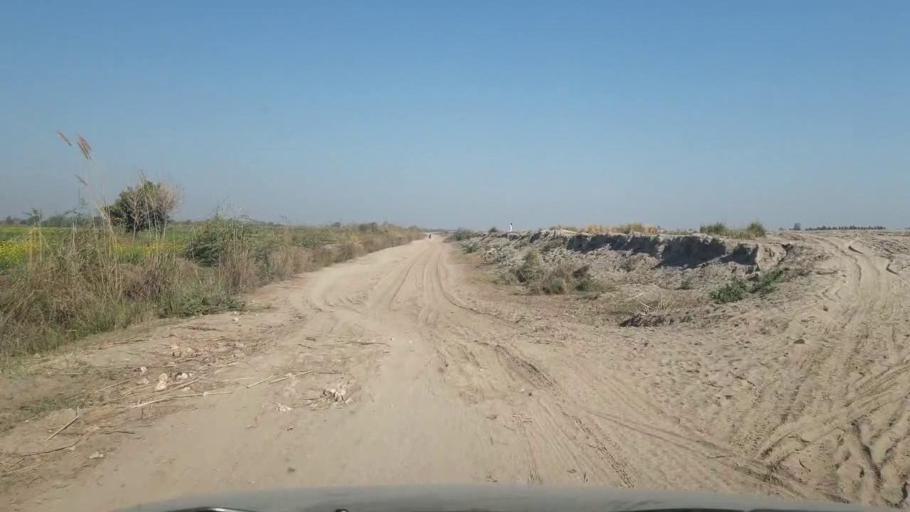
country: PK
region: Sindh
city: Mirwah Gorchani
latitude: 25.3349
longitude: 69.1019
